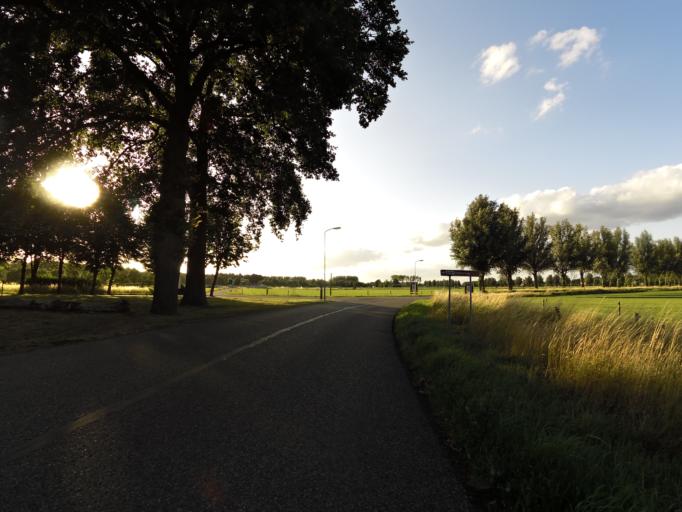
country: NL
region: Gelderland
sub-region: Gemeente Doetinchem
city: Doetinchem
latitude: 51.9869
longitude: 6.2866
